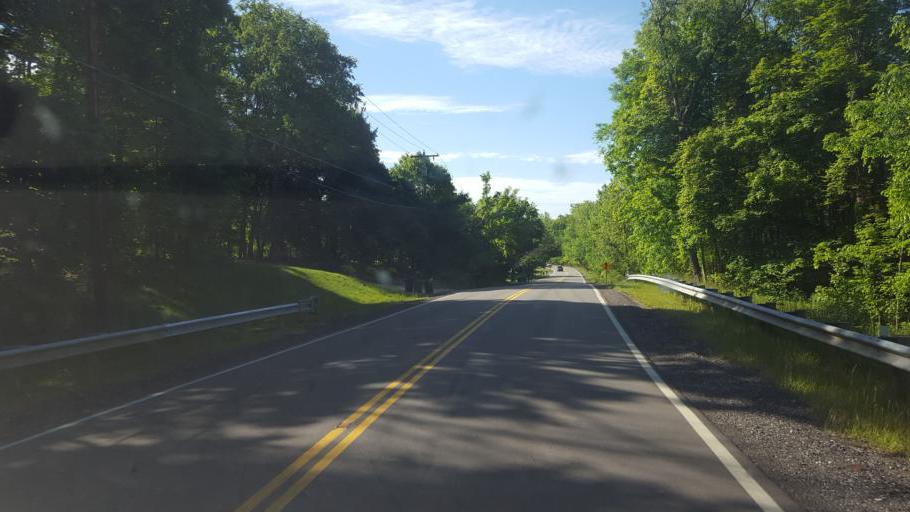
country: US
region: Ohio
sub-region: Medina County
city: Medina
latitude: 41.1062
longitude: -81.7906
